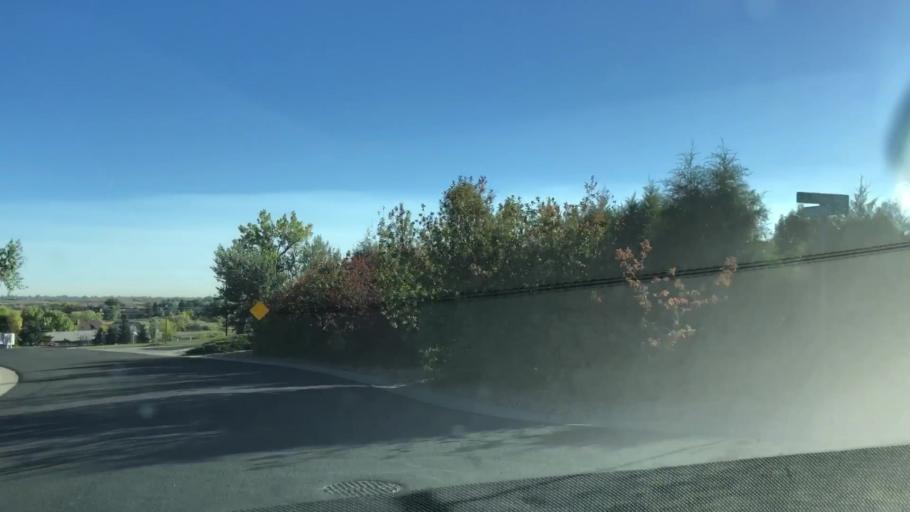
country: US
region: Colorado
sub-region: Larimer County
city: Loveland
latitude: 40.3783
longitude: -105.1447
